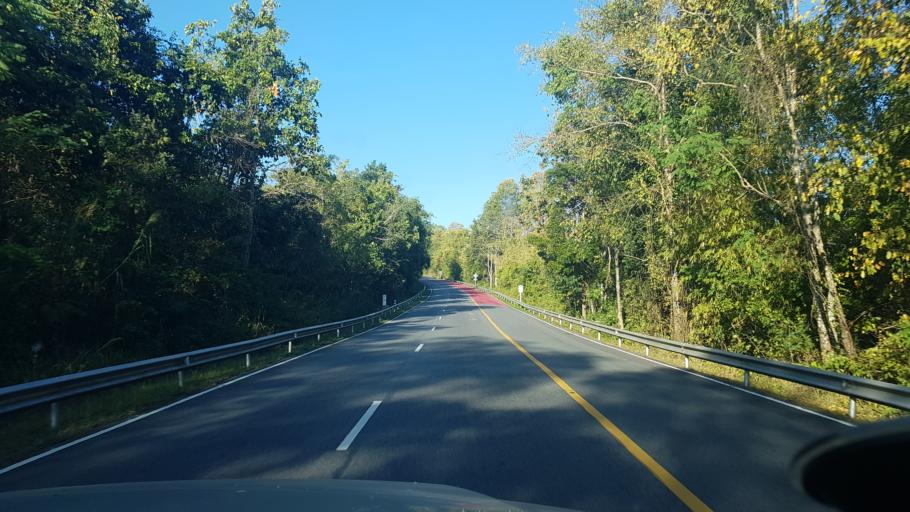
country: TH
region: Phetchabun
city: Nam Nao
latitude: 16.7029
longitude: 101.6591
